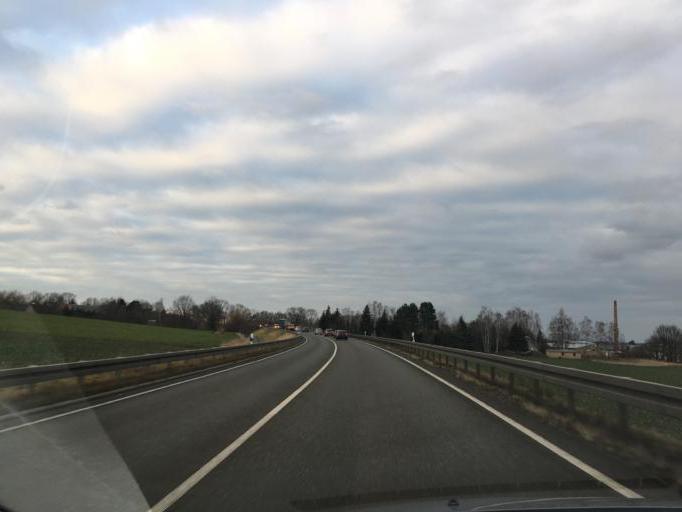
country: DE
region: Thuringia
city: Nobitz
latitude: 50.9983
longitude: 12.4710
